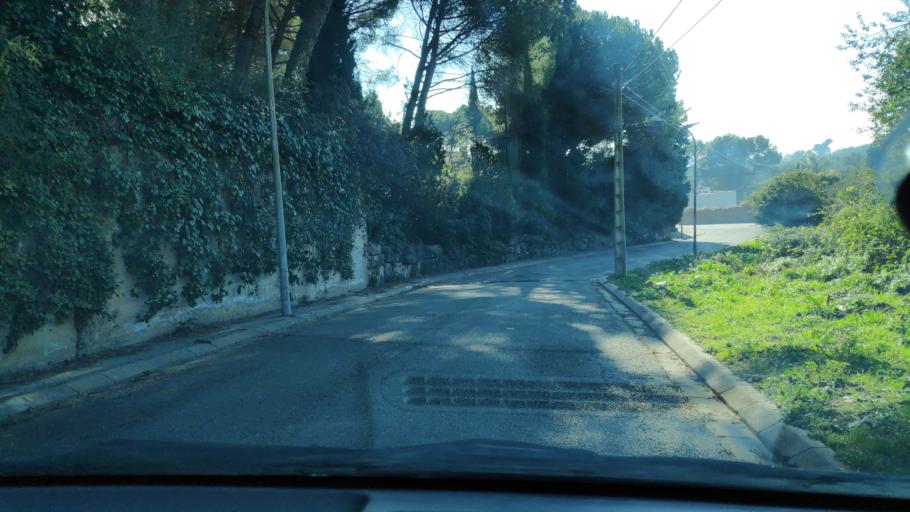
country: ES
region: Catalonia
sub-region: Provincia de Barcelona
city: Sant Quirze del Valles
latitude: 41.5019
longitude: 2.0786
